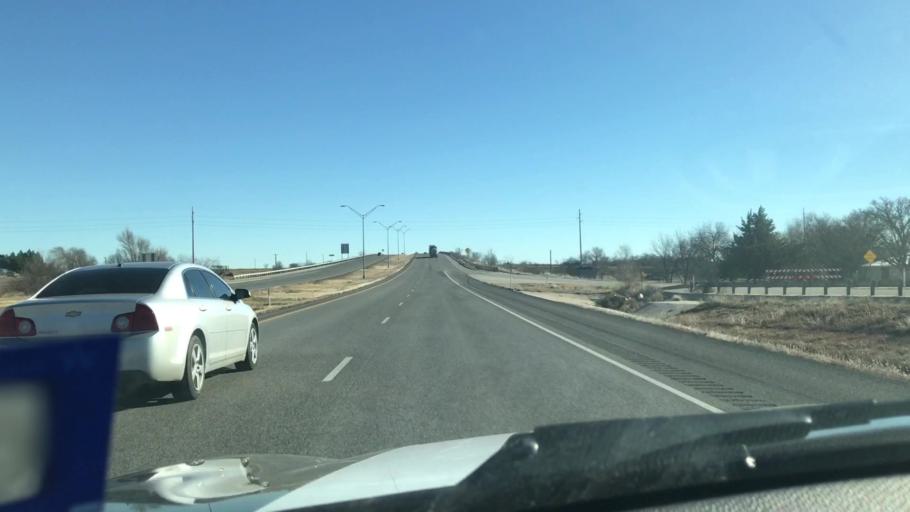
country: US
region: Texas
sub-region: Scurry County
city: Snyder
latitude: 32.7029
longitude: -100.8672
